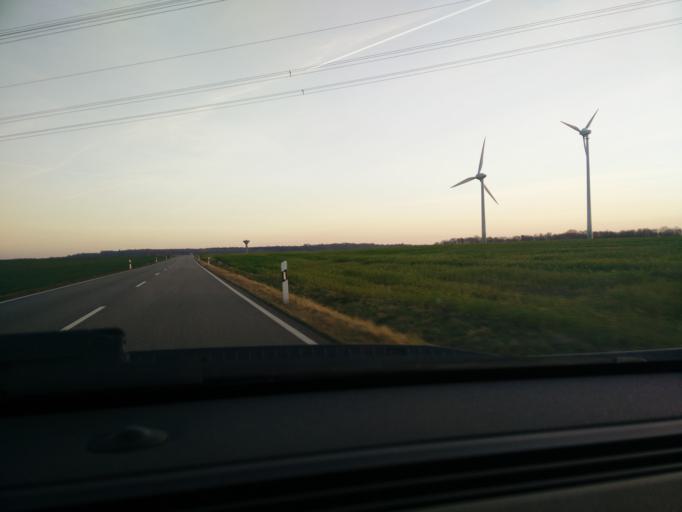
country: DE
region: Saxony
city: Geithain
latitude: 51.0958
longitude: 12.7013
